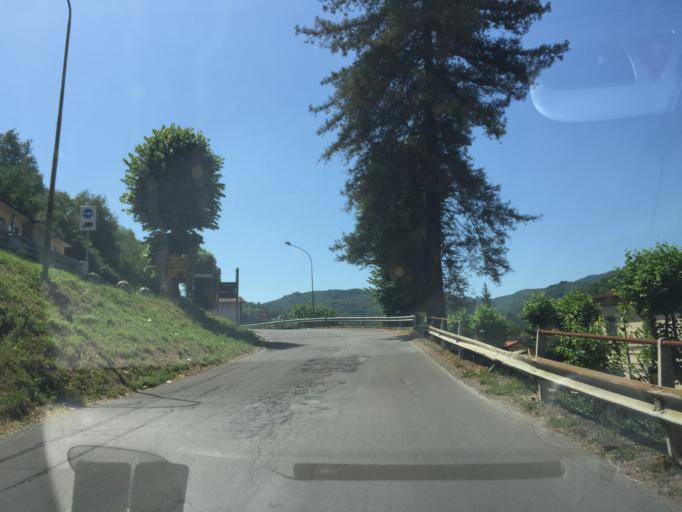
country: IT
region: Tuscany
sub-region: Provincia di Lucca
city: Castelnuovo di Garfagnana
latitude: 44.1171
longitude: 10.4097
